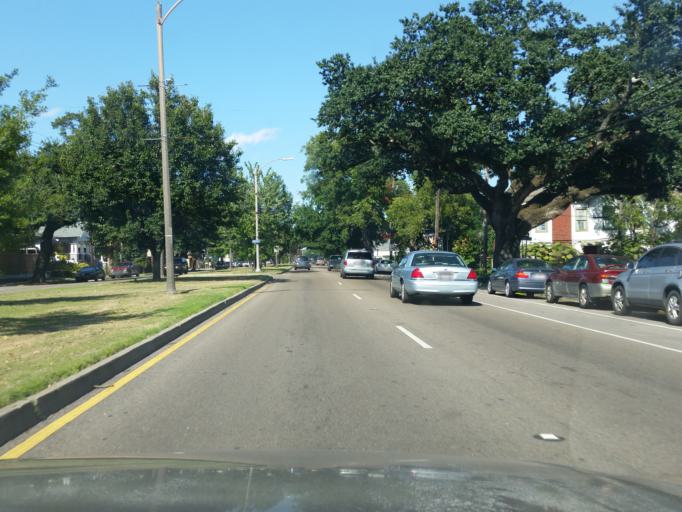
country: US
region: Louisiana
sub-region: Orleans Parish
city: New Orleans
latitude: 29.9796
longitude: -90.0749
